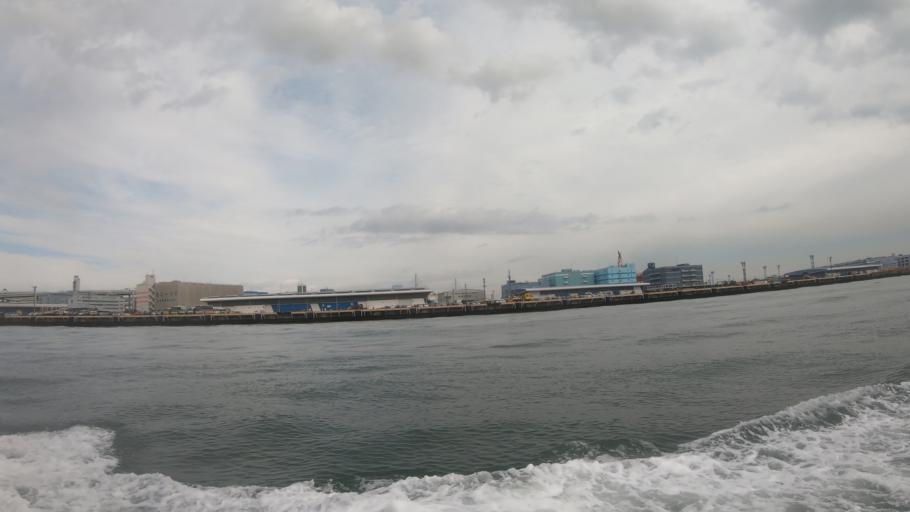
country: JP
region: Kanagawa
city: Yokohama
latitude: 35.4544
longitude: 139.6828
